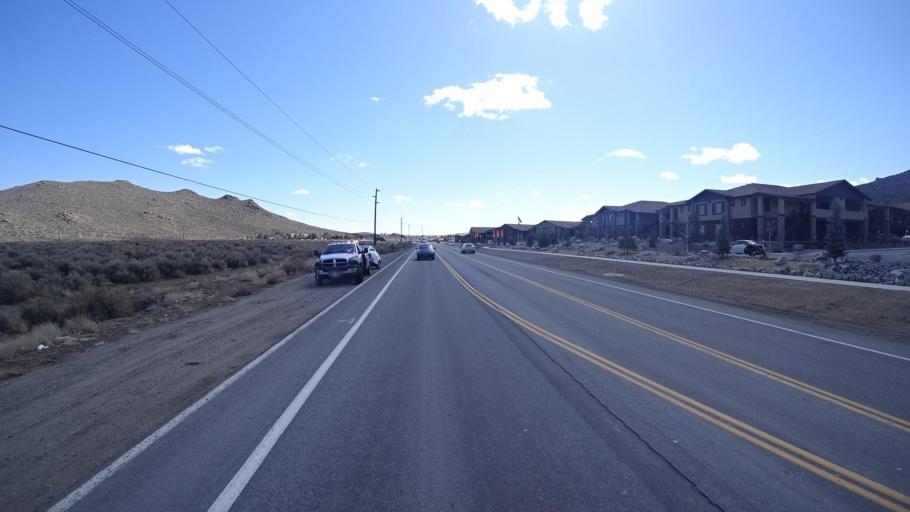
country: US
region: Nevada
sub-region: Washoe County
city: Lemmon Valley
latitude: 39.6269
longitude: -119.8510
